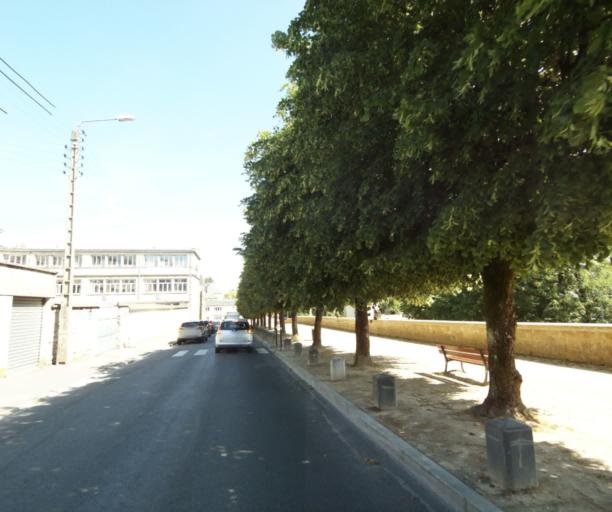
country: FR
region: Champagne-Ardenne
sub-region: Departement des Ardennes
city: Charleville-Mezieres
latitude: 49.7607
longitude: 4.7147
